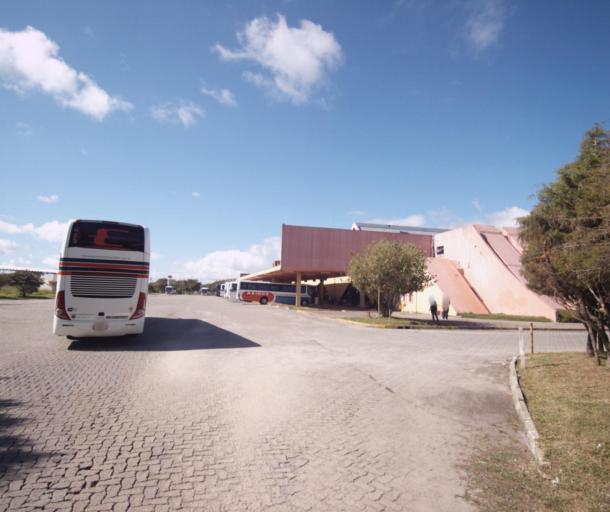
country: BR
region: Rio Grande do Sul
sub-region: Pelotas
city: Pelotas
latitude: -31.7549
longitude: -52.3595
